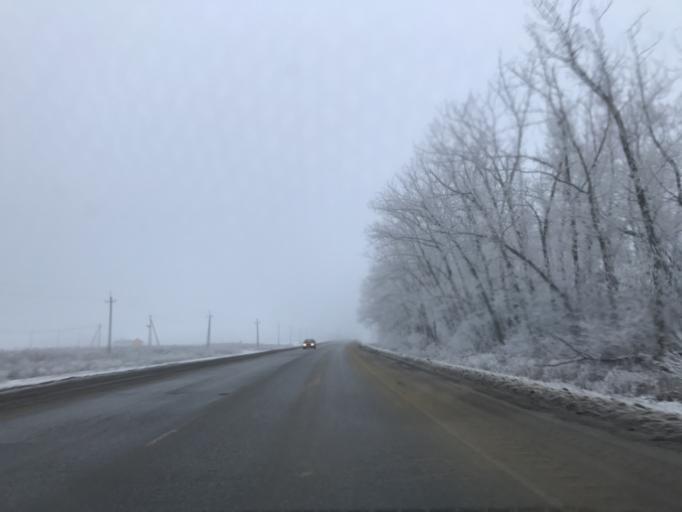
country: RU
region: Rostov
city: Temernik
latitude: 47.3774
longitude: 39.8073
